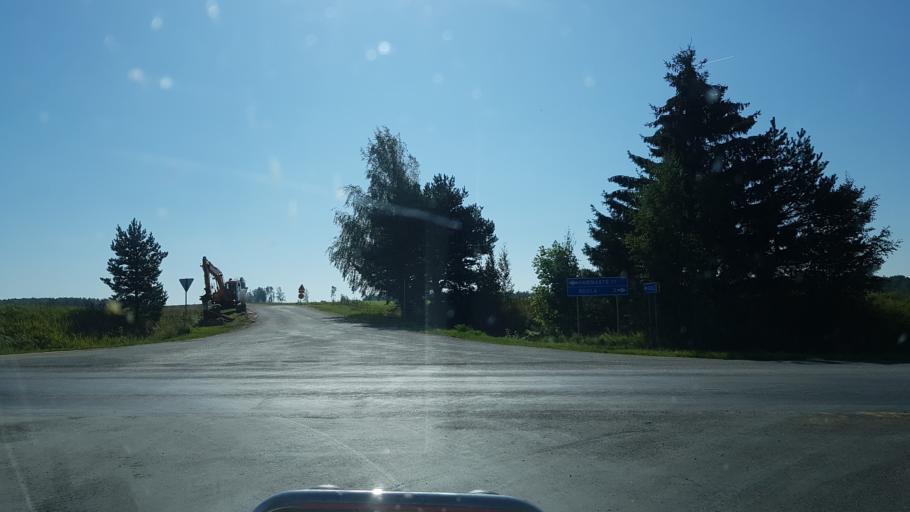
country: EE
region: Tartu
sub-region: UElenurme vald
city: Ulenurme
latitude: 58.2797
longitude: 26.8195
